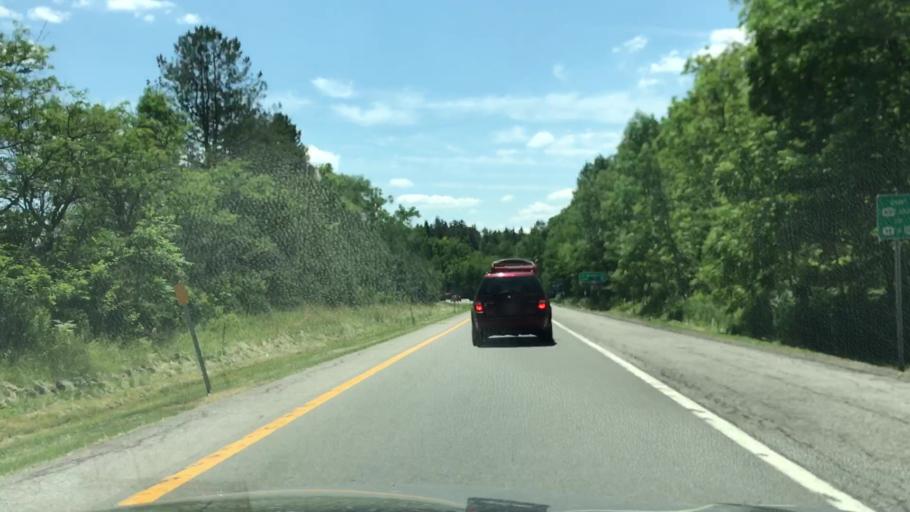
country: US
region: New York
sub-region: Erie County
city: East Aurora
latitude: 42.7697
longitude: -78.5931
